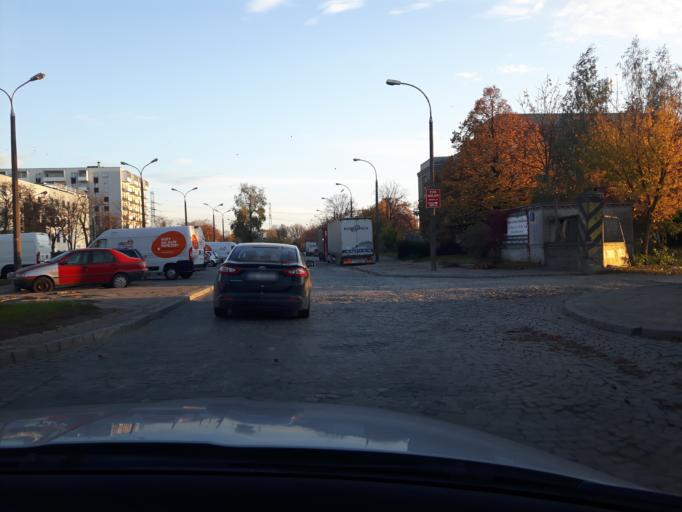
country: PL
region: Masovian Voivodeship
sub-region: Warszawa
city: Ochota
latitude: 52.2232
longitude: 20.9537
